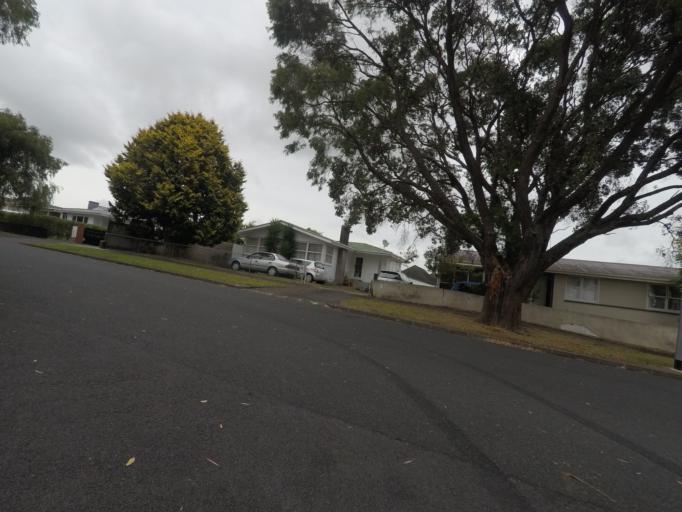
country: NZ
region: Auckland
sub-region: Auckland
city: Rosebank
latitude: -36.8861
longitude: 174.6763
